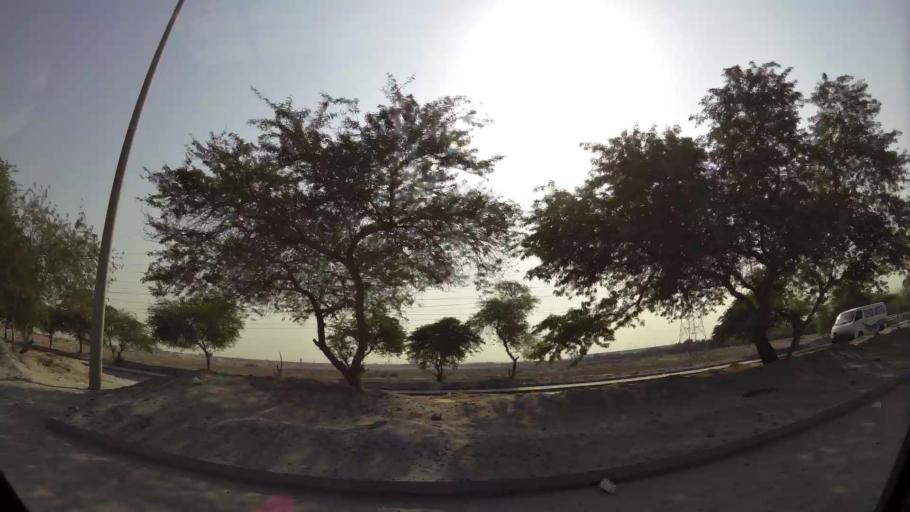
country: KW
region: Al Asimah
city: Ar Rabiyah
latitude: 29.2798
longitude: 47.8431
